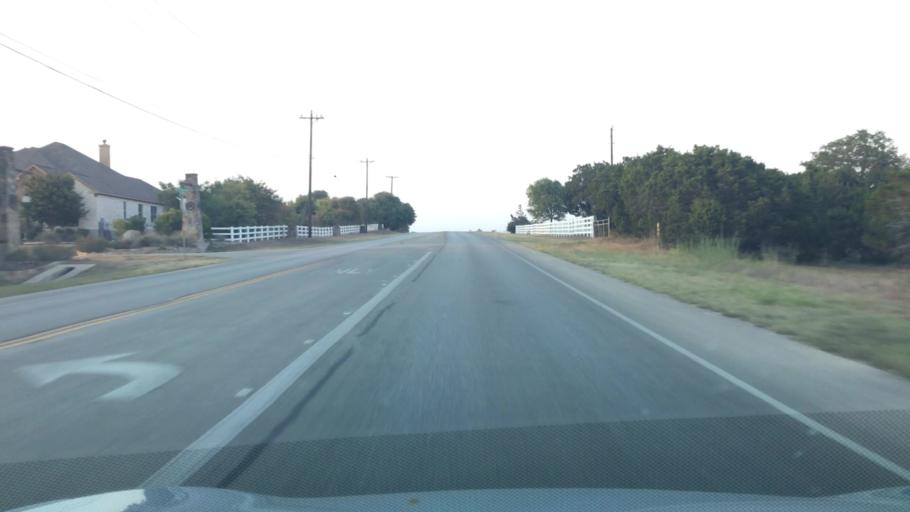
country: US
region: Texas
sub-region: Hays County
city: Dripping Springs
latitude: 30.1825
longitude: -98.0017
